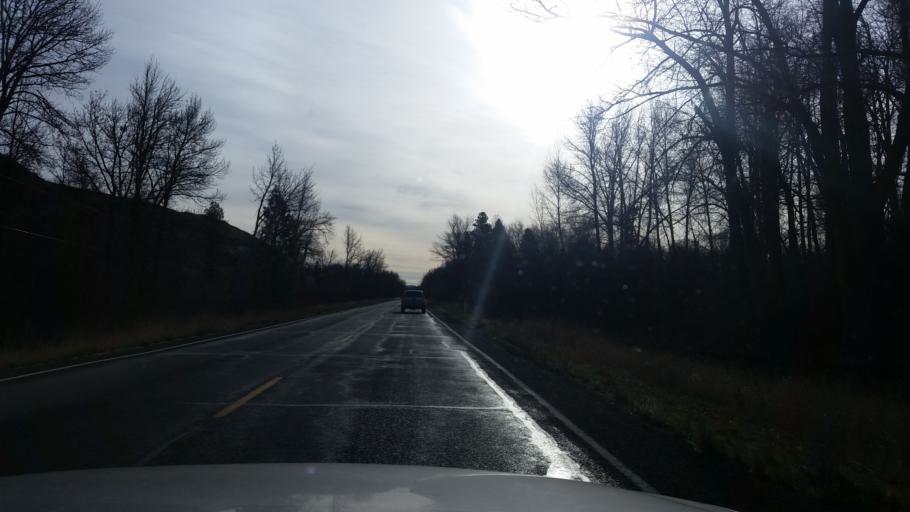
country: US
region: Washington
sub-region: Kittitas County
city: Ellensburg
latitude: 47.0672
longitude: -120.6535
